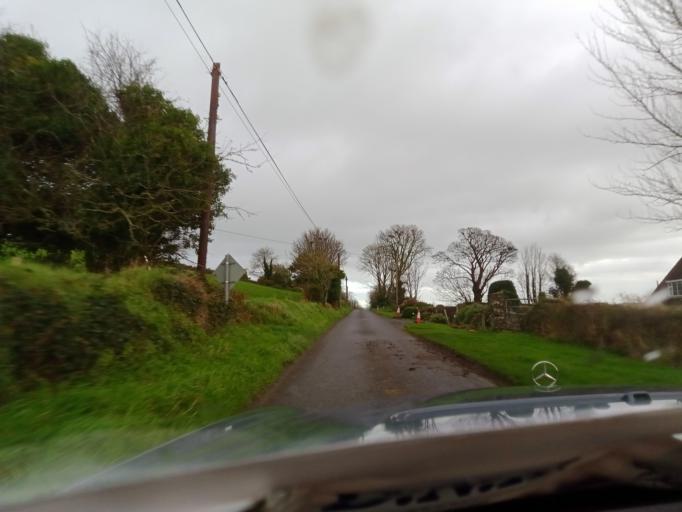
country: IE
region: Leinster
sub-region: Kilkenny
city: Mooncoin
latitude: 52.2651
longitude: -7.1935
